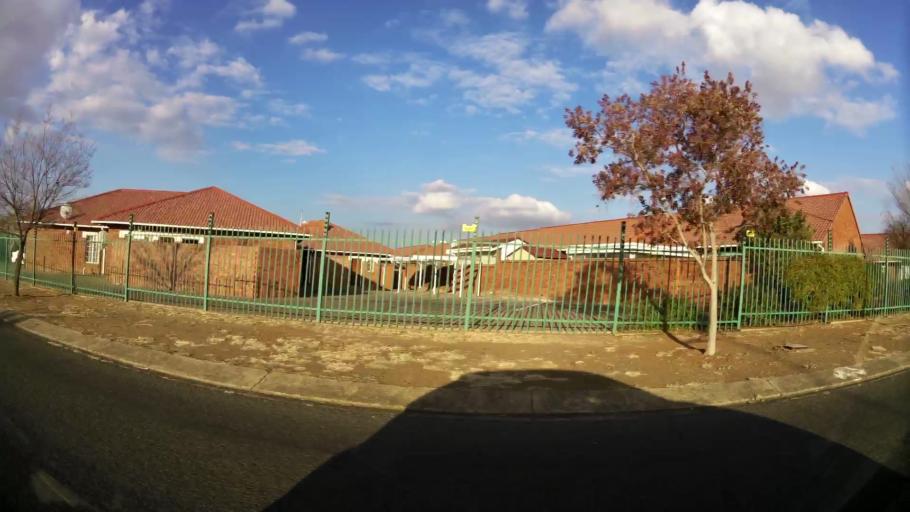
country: ZA
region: Orange Free State
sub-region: Mangaung Metropolitan Municipality
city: Bloemfontein
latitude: -29.1494
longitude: 26.1868
